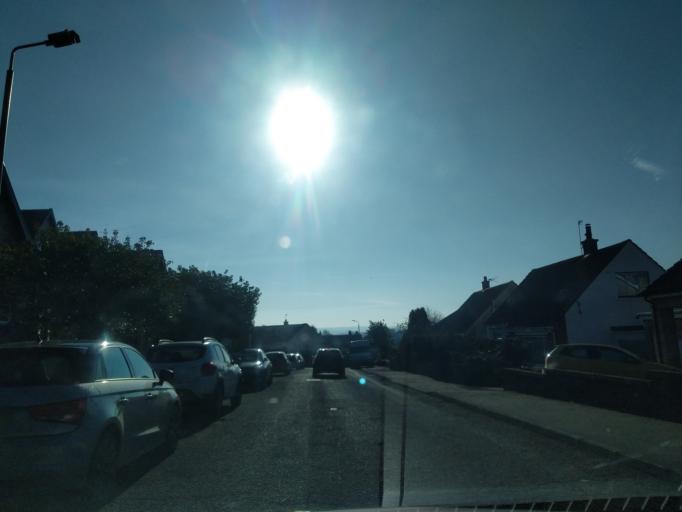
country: GB
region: Scotland
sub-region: South Lanarkshire
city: Lanark
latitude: 55.6706
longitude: -3.7757
